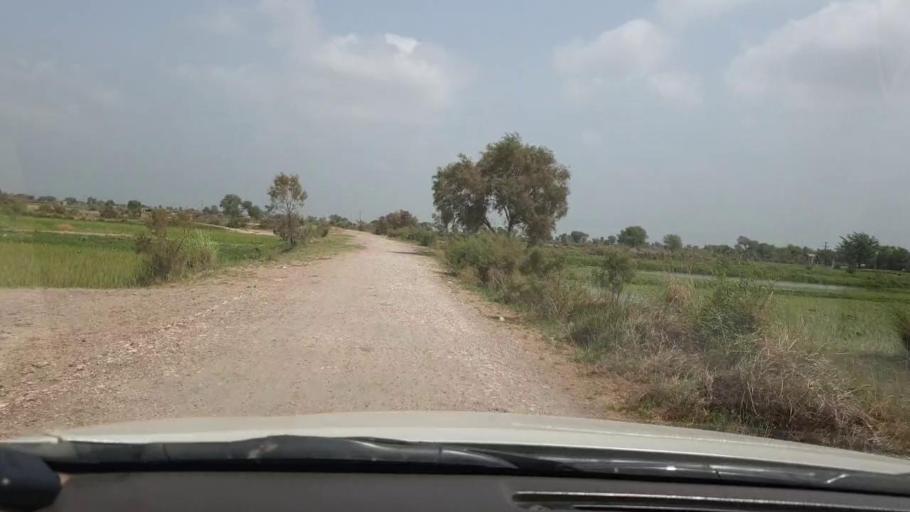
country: PK
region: Sindh
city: Garhi Yasin
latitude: 28.0162
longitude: 68.5286
